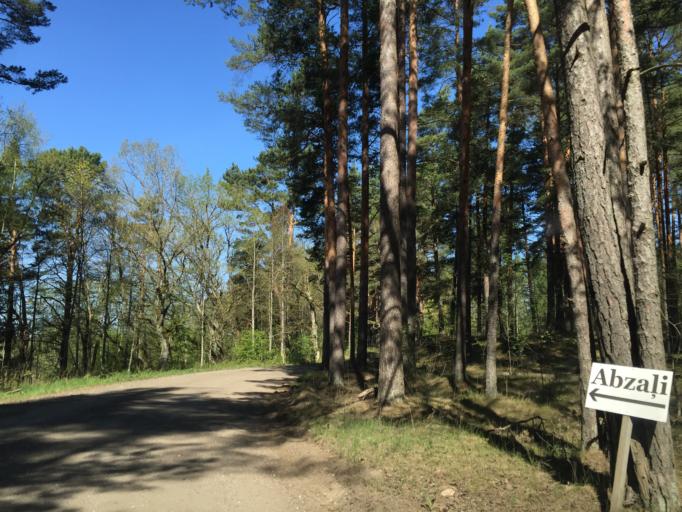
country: LV
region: Adazi
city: Adazi
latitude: 57.0907
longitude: 24.3401
